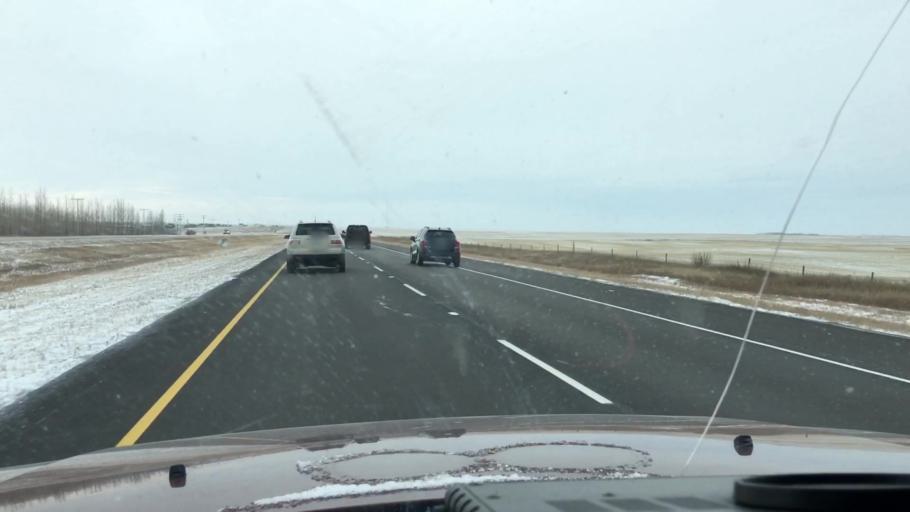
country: CA
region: Saskatchewan
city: Saskatoon
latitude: 51.7695
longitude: -106.4763
